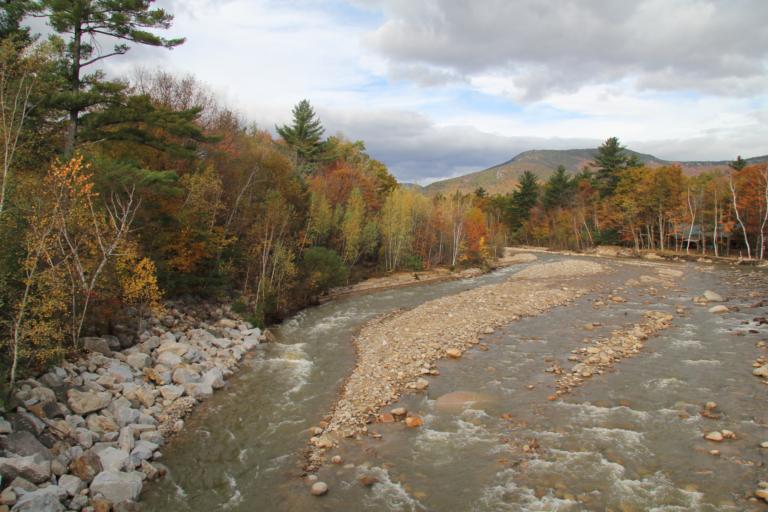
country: US
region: New Hampshire
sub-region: Carroll County
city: North Conway
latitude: 44.1032
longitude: -71.1997
